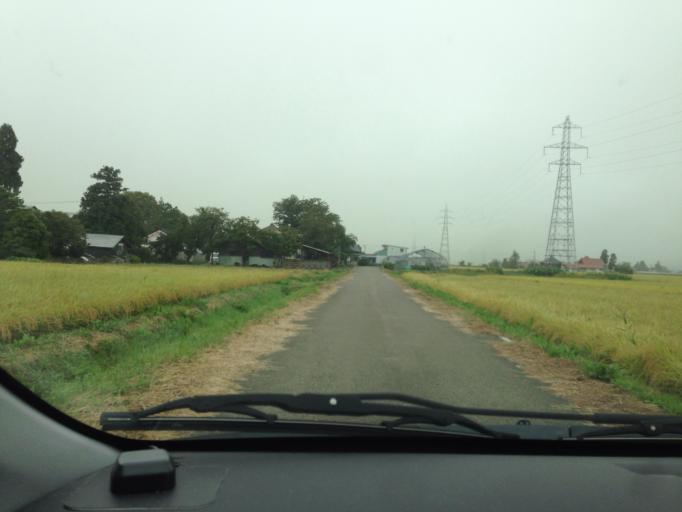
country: JP
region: Fukushima
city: Kitakata
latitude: 37.5746
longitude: 139.8424
